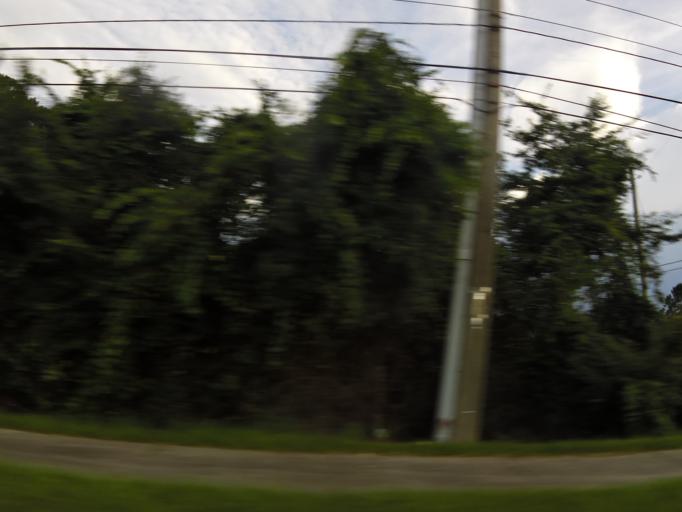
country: US
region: Florida
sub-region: Duval County
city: Jacksonville
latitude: 30.3715
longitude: -81.7897
